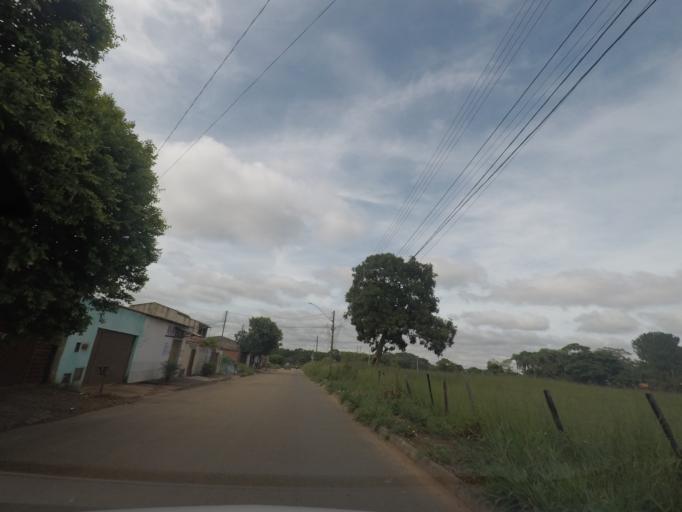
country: BR
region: Goias
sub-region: Goiania
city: Goiania
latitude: -16.6711
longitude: -49.1846
